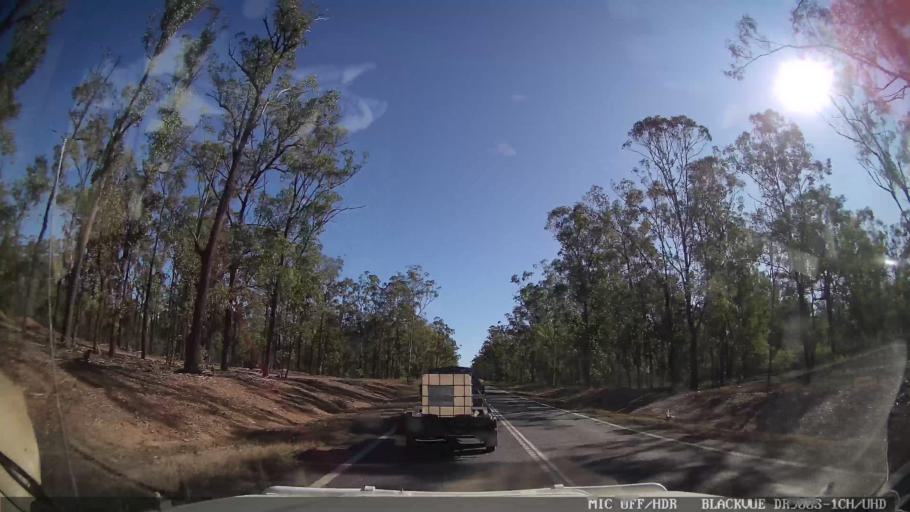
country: AU
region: Queensland
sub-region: Bundaberg
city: Childers
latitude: -25.2161
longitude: 152.0753
